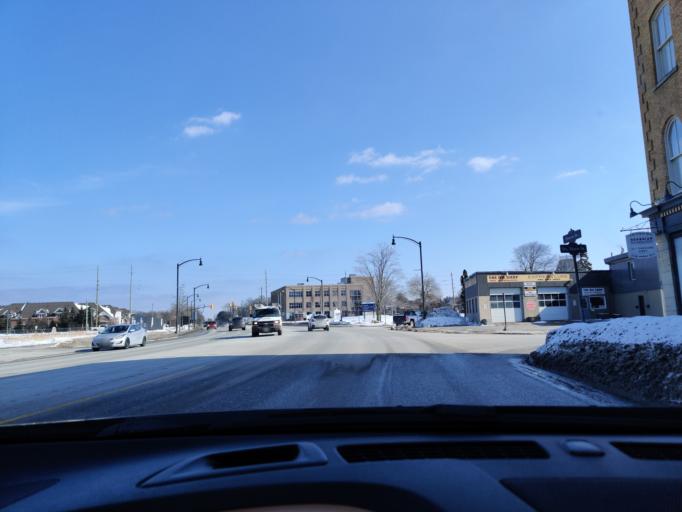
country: CA
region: Ontario
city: Collingwood
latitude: 44.5029
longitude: -80.2162
